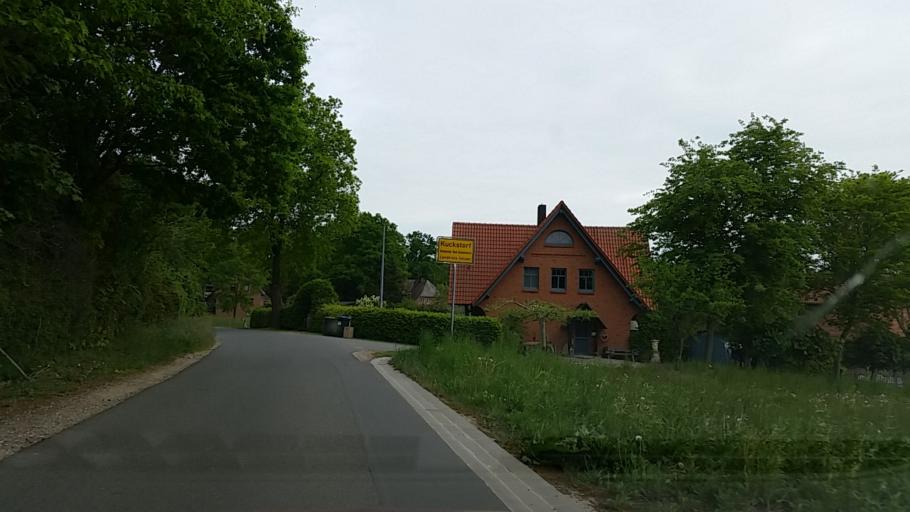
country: DE
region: Lower Saxony
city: Wieren
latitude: 52.8603
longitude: 10.6700
